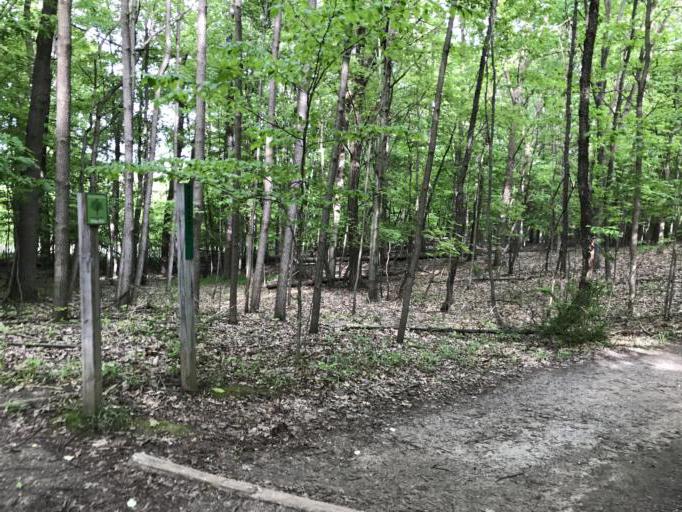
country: US
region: Michigan
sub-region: Oakland County
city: Farmington Hills
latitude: 42.4782
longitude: -83.3882
